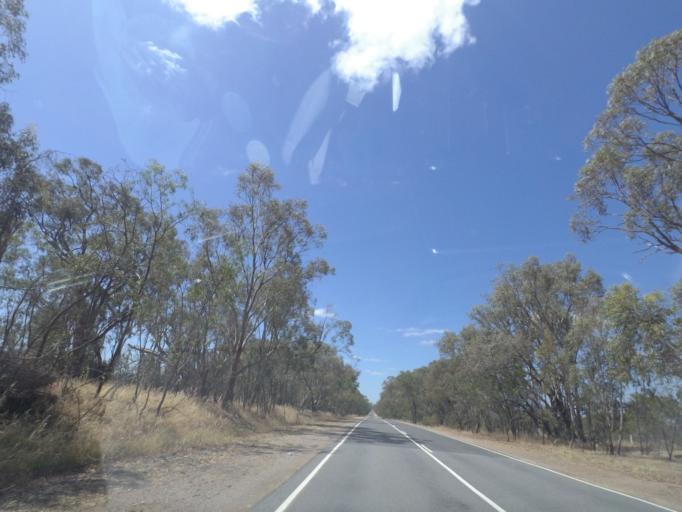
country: AU
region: Victoria
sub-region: Wangaratta
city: Wangaratta
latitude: -36.4436
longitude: 146.2435
